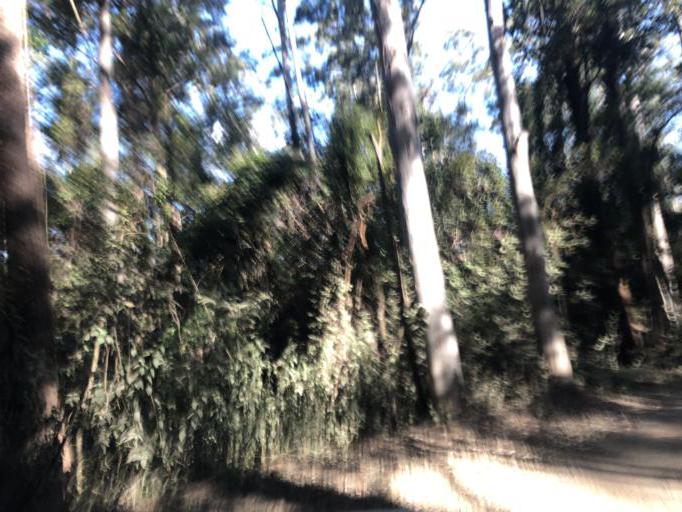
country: AU
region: New South Wales
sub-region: Bellingen
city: Bellingen
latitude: -30.4368
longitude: 152.8328
